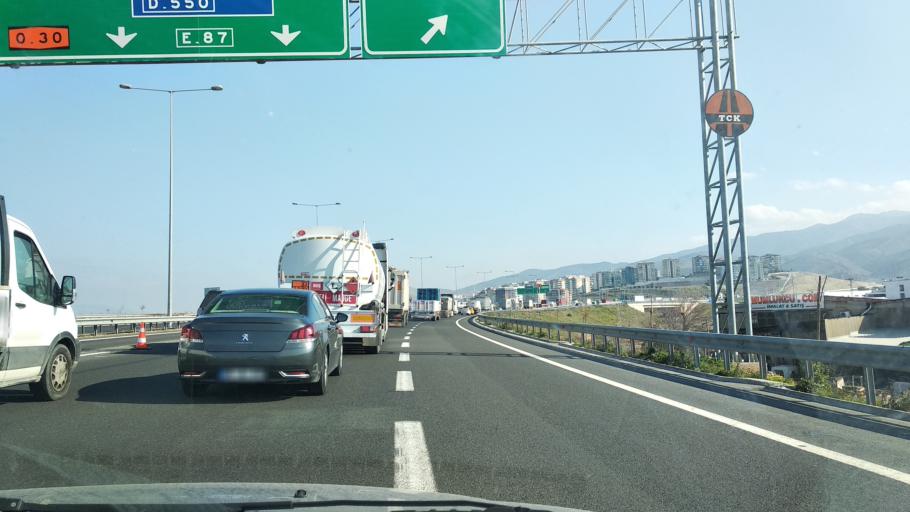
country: TR
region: Izmir
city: Menemen
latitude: 38.5705
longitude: 27.0499
